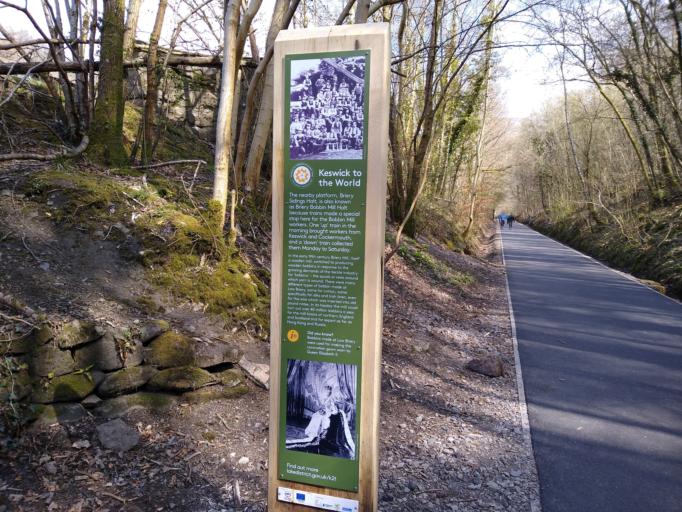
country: GB
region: England
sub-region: Cumbria
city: Keswick
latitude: 54.6075
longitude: -3.1070
